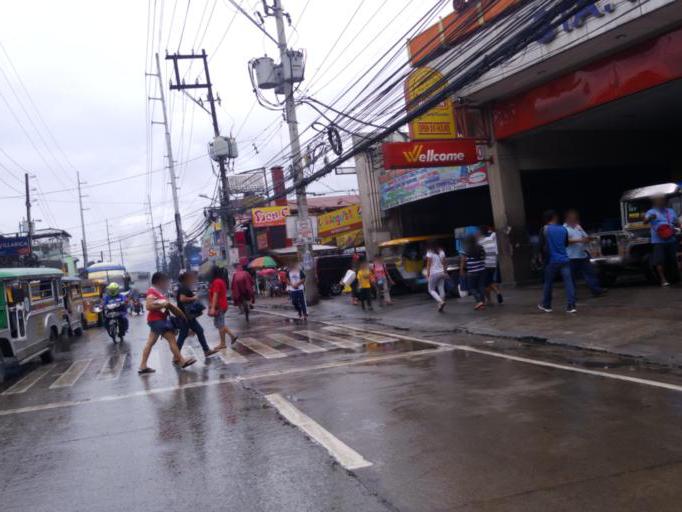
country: PH
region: Calabarzon
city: Bagong Pagasa
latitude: 14.7230
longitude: 121.0415
